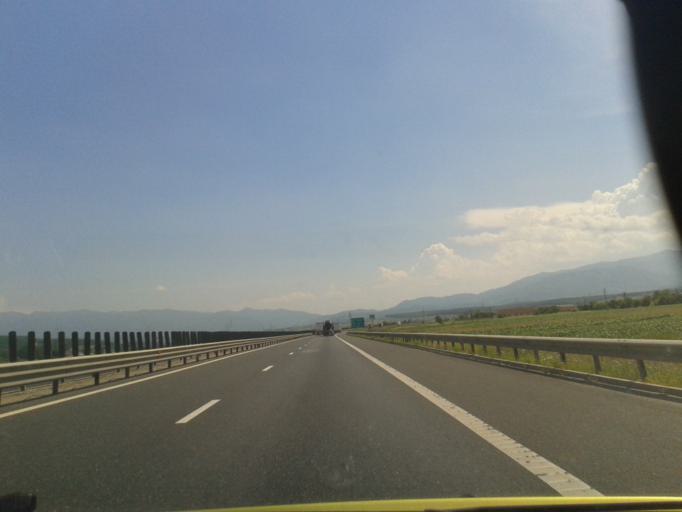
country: RO
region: Sibiu
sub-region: Comuna Selimbar
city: Selimbar
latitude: 45.7682
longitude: 24.2059
